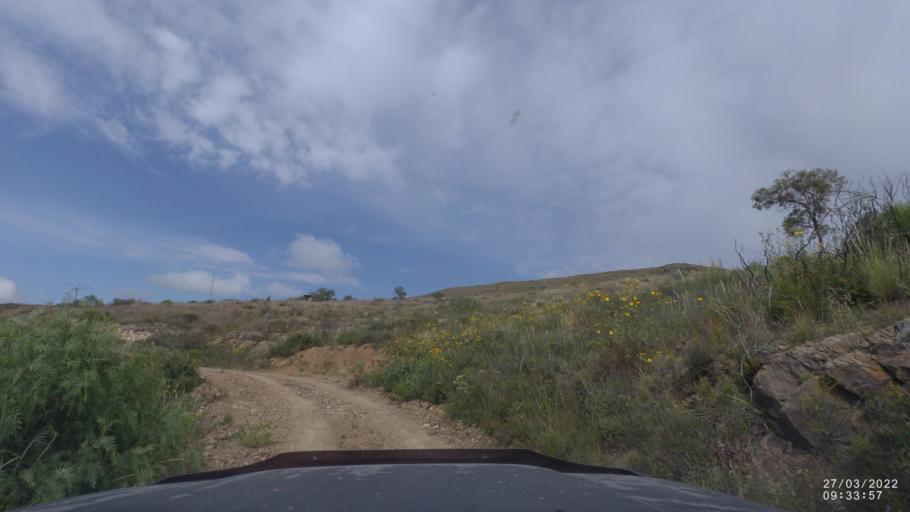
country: BO
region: Cochabamba
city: Cliza
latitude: -17.7409
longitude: -65.8908
